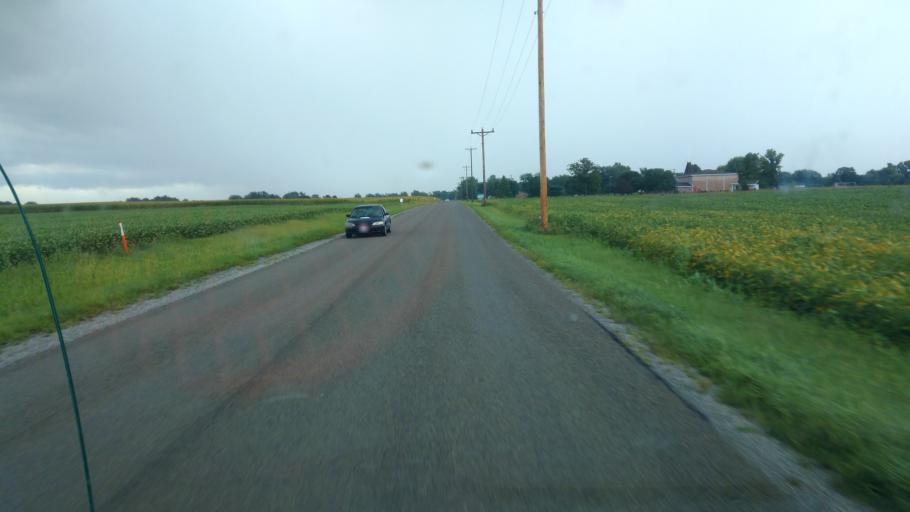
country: US
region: Ohio
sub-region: Hardin County
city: Kenton
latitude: 40.6536
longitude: -83.5762
